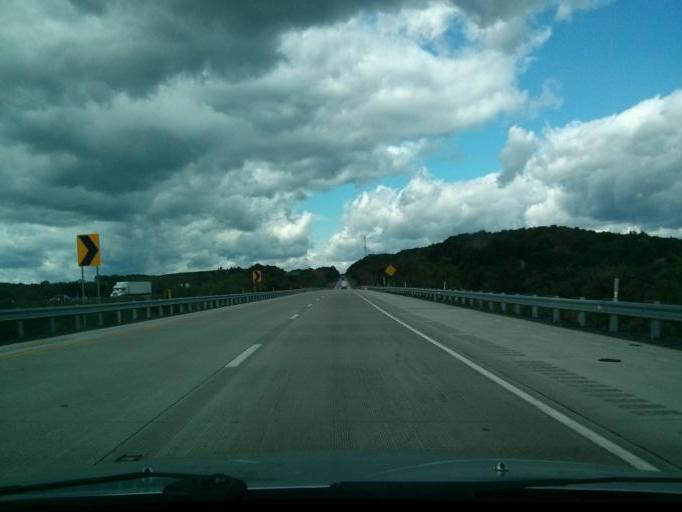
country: US
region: Pennsylvania
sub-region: Jefferson County
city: Falls Creek
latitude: 41.1494
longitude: -78.8534
